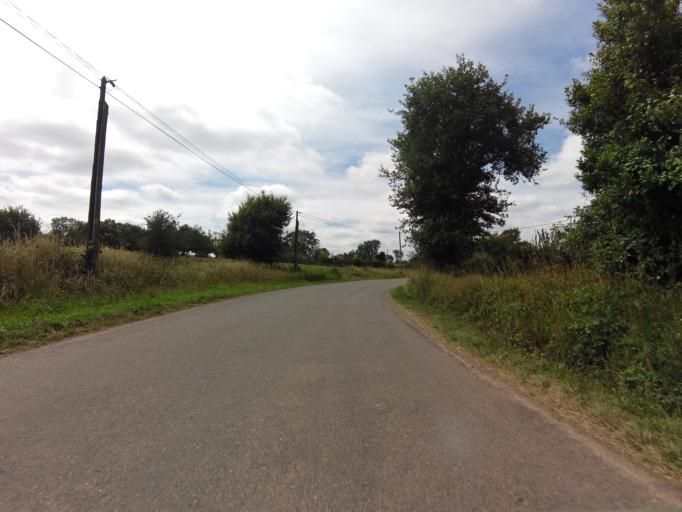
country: FR
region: Brittany
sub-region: Departement du Morbihan
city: Mauron
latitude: 48.0208
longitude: -2.2769
